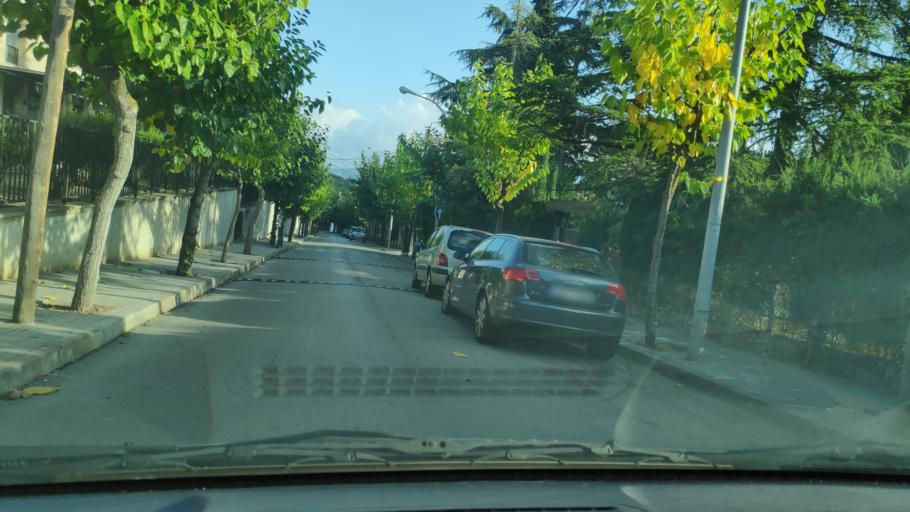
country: ES
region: Catalonia
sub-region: Provincia de Barcelona
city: Sant Quirze del Valles
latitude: 41.5024
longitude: 2.0861
